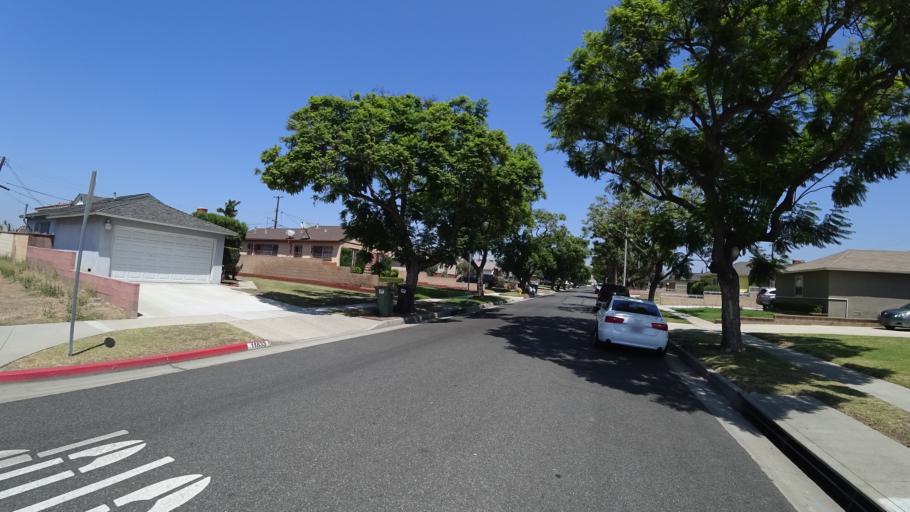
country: US
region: California
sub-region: Los Angeles County
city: West Athens
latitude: 33.9261
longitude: -118.3236
